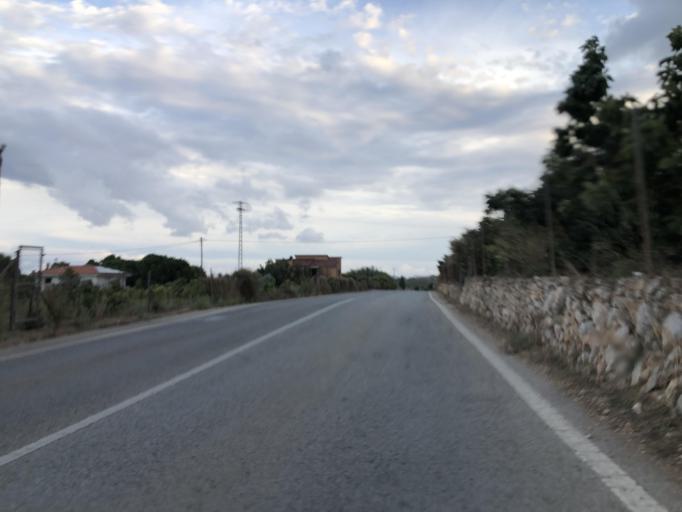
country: ES
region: Valencia
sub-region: Provincia de Alicante
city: Polop
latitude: 38.6294
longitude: -0.1415
